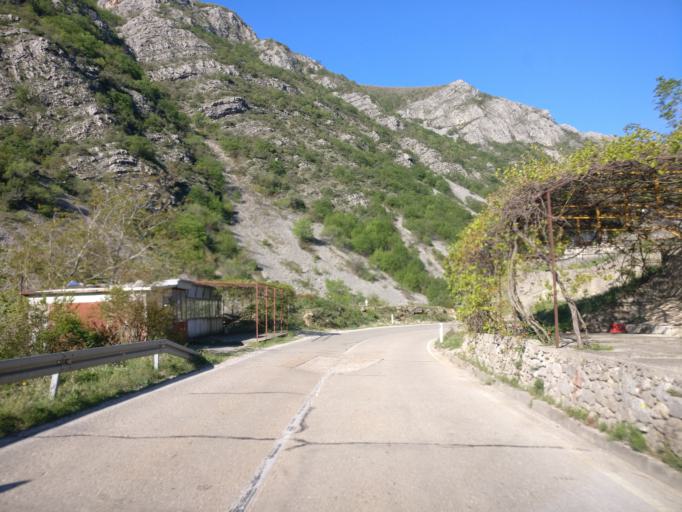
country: BA
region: Federation of Bosnia and Herzegovina
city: Stolac
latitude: 43.0786
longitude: 18.0177
